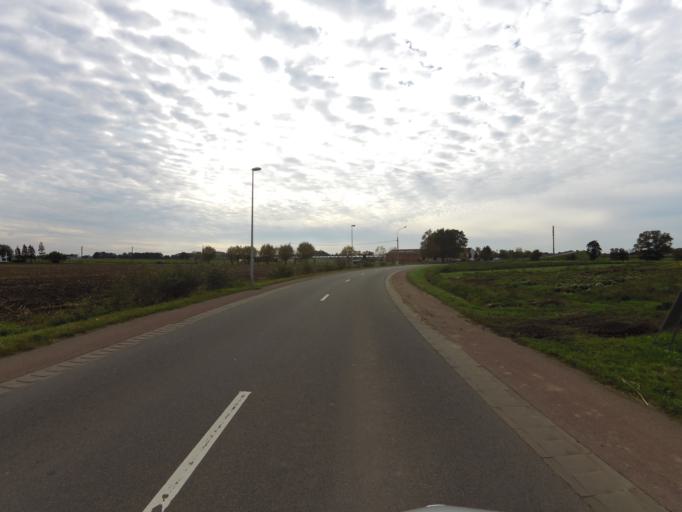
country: BE
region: Flanders
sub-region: Provincie West-Vlaanderen
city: Lichtervelde
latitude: 51.0695
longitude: 3.1605
